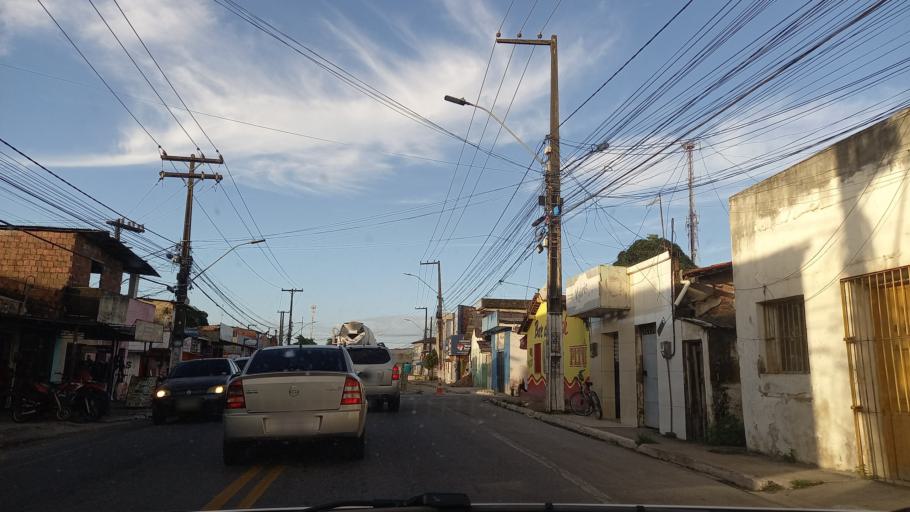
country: BR
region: Pernambuco
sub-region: Jaboatao Dos Guararapes
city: Jaboatao
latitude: -8.2252
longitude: -34.9675
